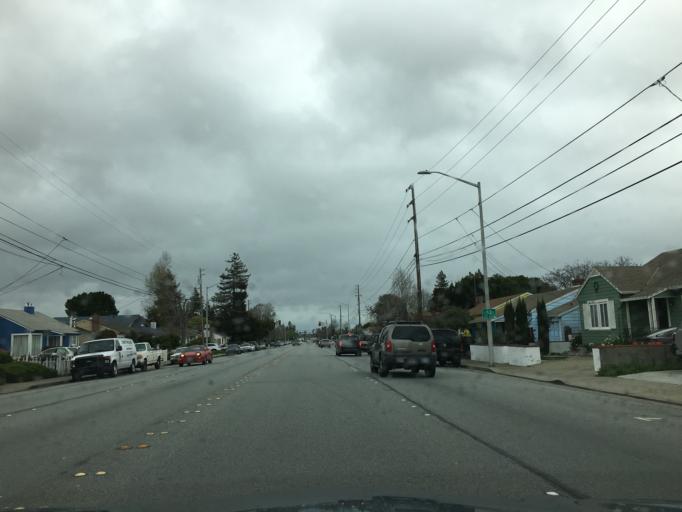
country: US
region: California
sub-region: San Mateo County
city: Belmont
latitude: 37.5385
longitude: -122.2954
